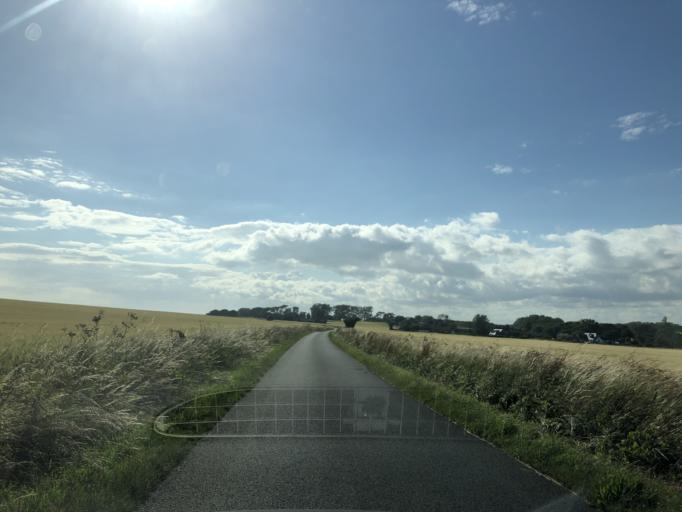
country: GB
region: England
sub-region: Isle of Wight
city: Shalfleet
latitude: 50.6891
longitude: -1.4390
